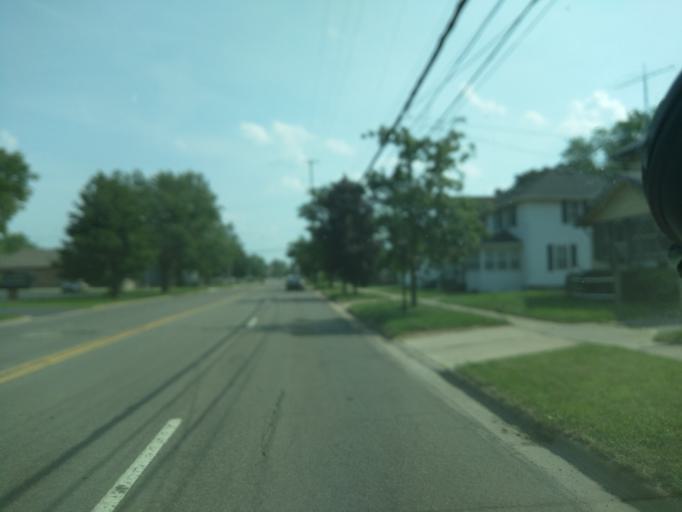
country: US
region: Michigan
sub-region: Jackson County
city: Jackson
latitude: 42.2566
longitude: -84.4284
